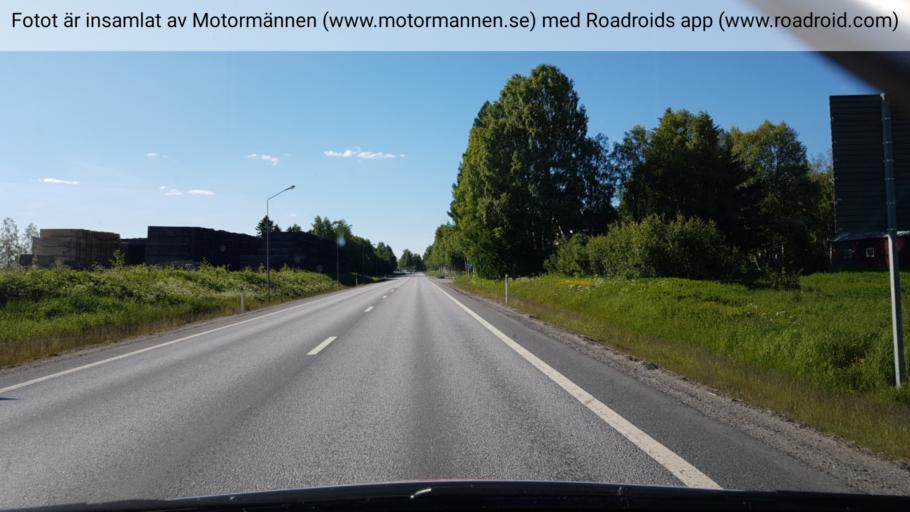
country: SE
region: Vaesterbotten
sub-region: Vannas Kommun
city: Vannasby
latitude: 63.9160
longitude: 19.8784
